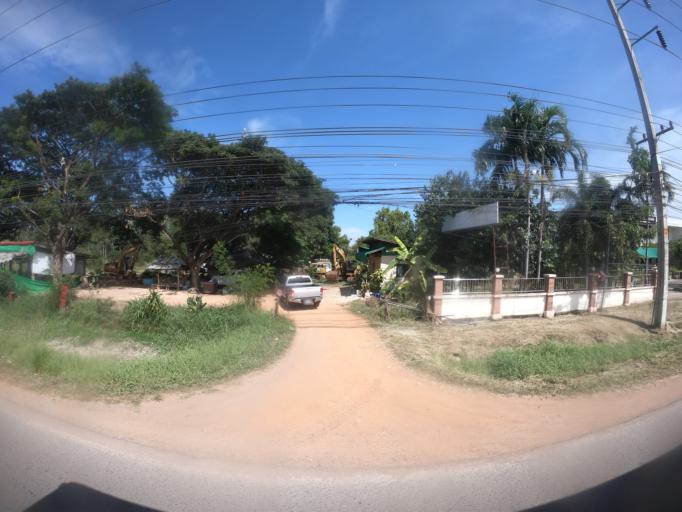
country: TH
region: Khon Kaen
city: Khon Kaen
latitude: 16.4379
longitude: 102.9348
